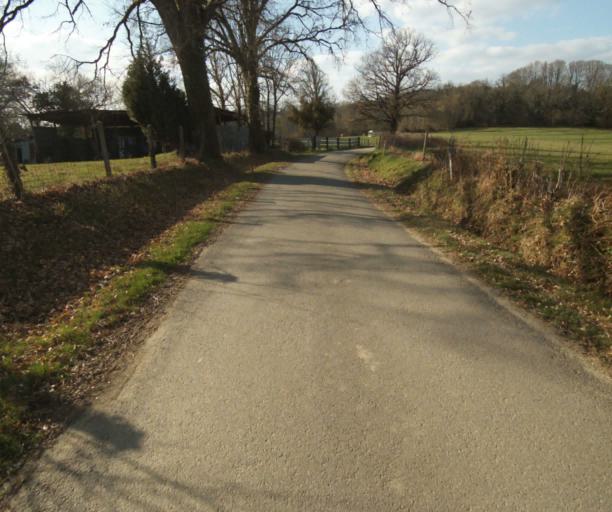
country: FR
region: Limousin
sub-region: Departement de la Correze
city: Saint-Mexant
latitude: 45.3383
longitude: 1.6083
